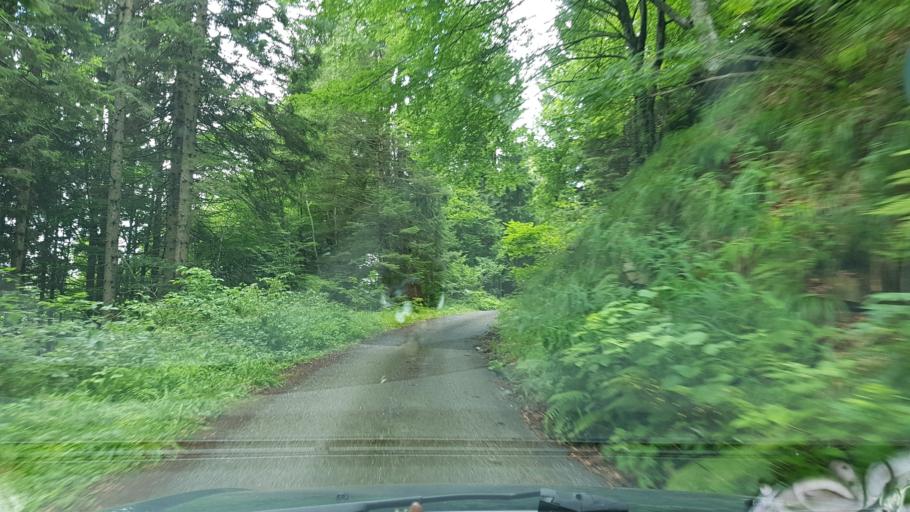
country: IT
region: Friuli Venezia Giulia
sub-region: Provincia di Udine
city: Cercivento
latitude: 46.5416
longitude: 12.9882
